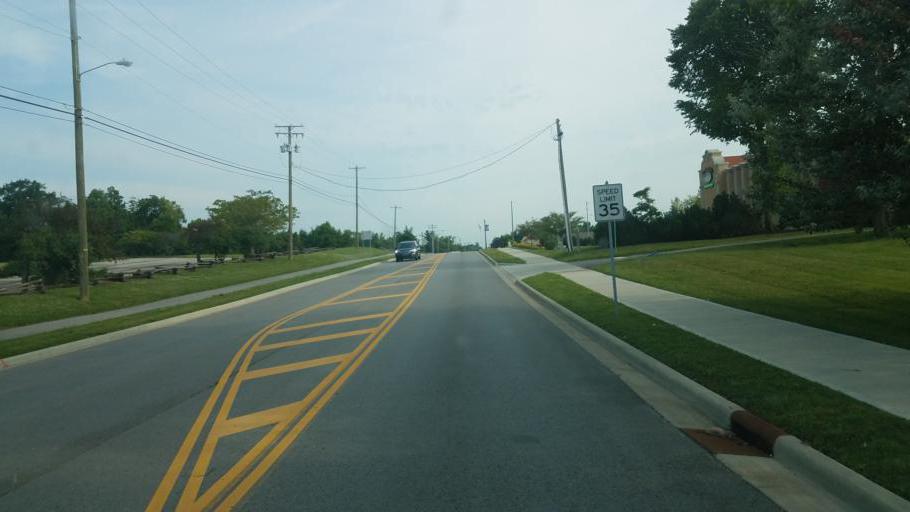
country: US
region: Ohio
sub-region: Delaware County
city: Powell
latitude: 40.1548
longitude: -83.1329
